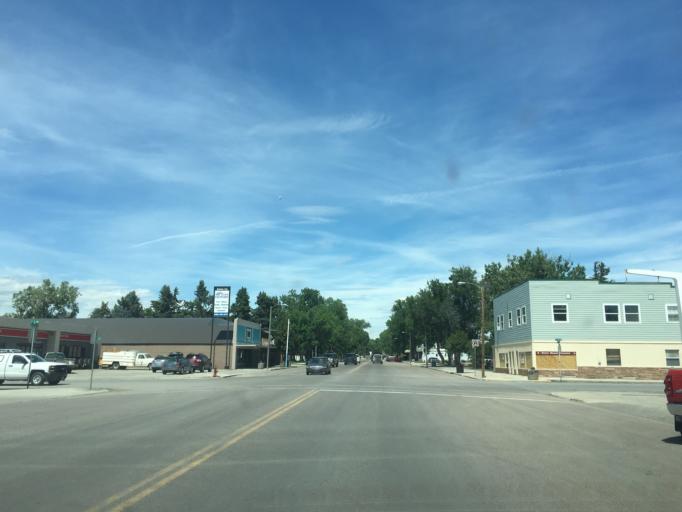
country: US
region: Montana
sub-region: Teton County
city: Choteau
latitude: 47.8136
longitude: -112.1846
